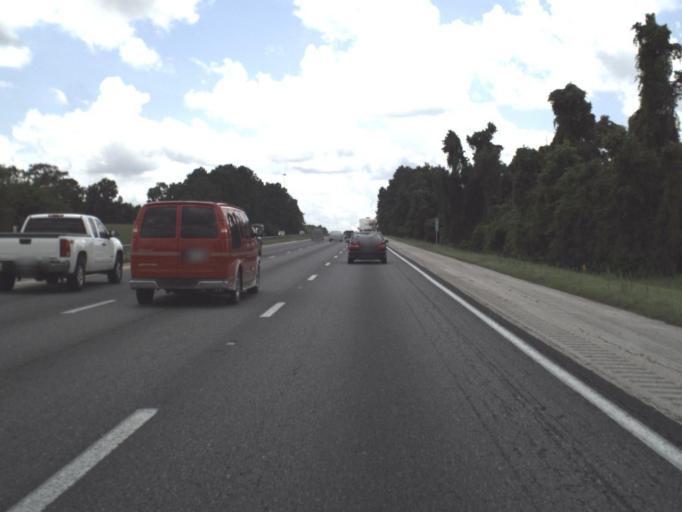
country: US
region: Florida
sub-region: Alachua County
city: High Springs
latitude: 29.8848
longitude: -82.5445
